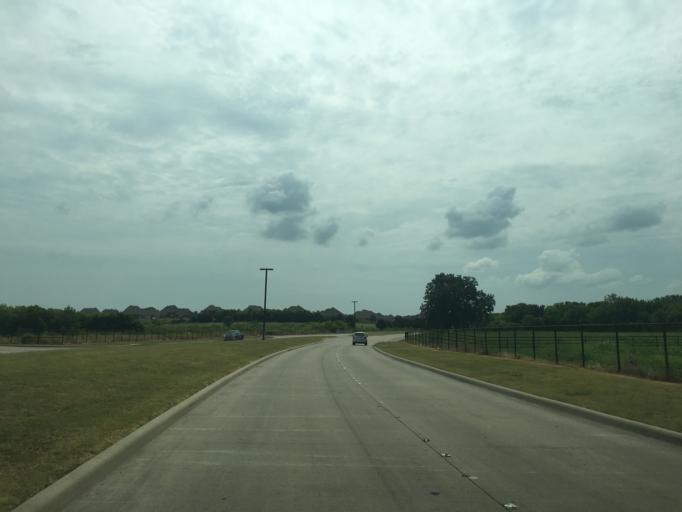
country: US
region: Texas
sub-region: Rockwall County
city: Rockwall
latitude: 32.9795
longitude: -96.4626
